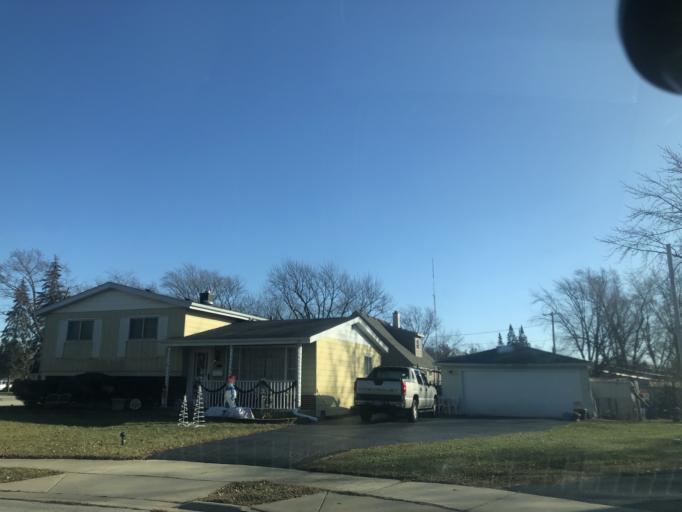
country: US
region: Illinois
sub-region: DuPage County
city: Addison
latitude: 41.9317
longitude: -88.0127
